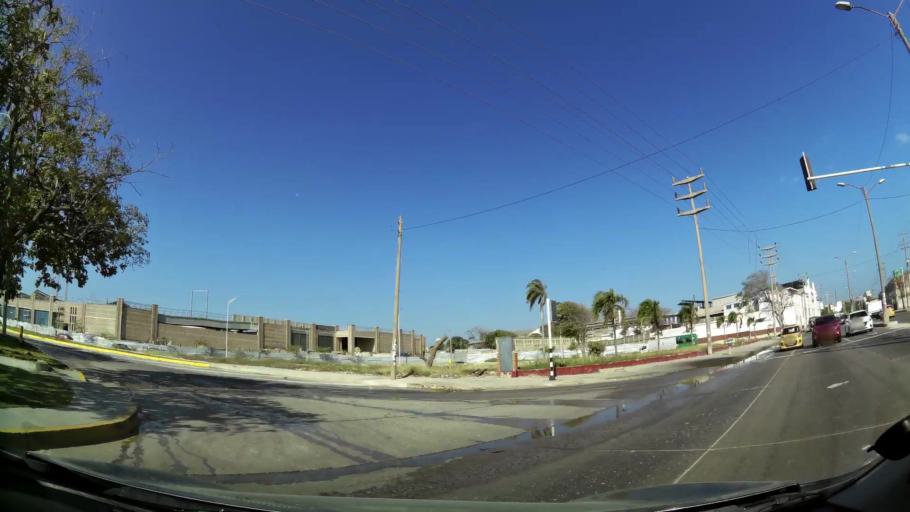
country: CO
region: Atlantico
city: Barranquilla
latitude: 10.9963
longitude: -74.7826
